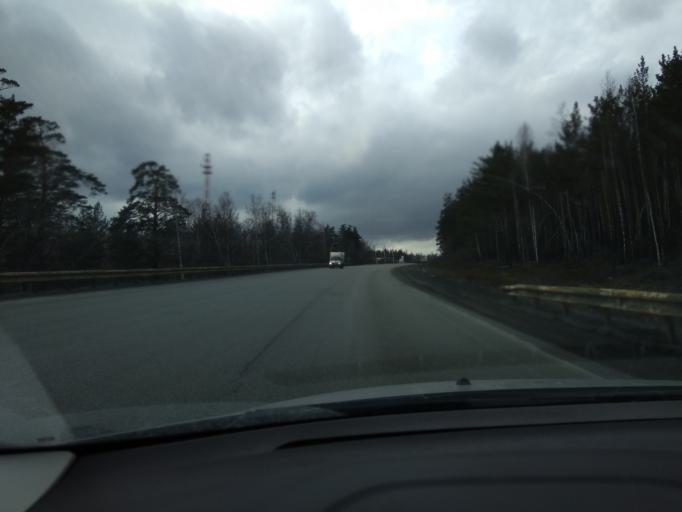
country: RU
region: Chelyabinsk
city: Syrostan
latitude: 55.0173
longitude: 59.7401
